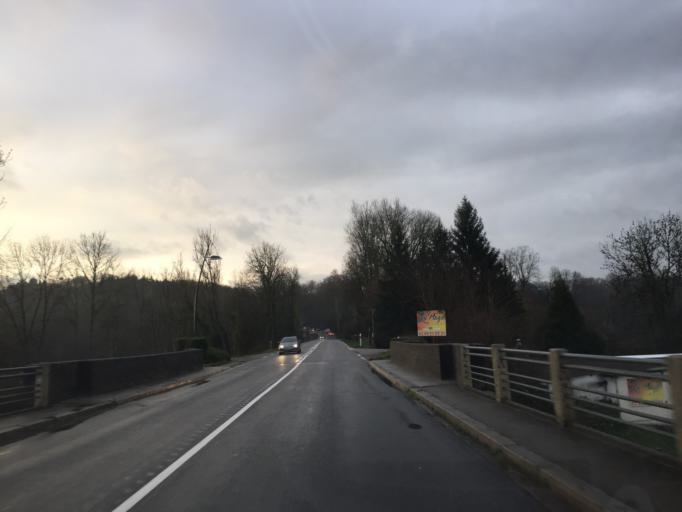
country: FR
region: Franche-Comte
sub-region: Departement du Jura
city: Choisey
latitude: 47.0150
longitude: 5.4946
